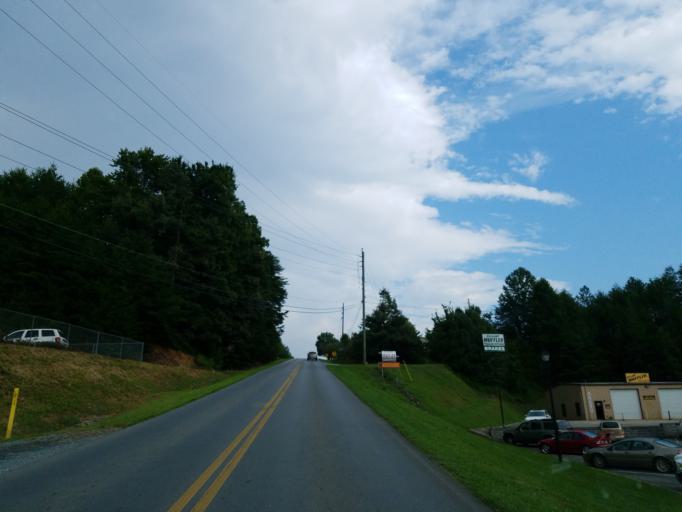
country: US
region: Georgia
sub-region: Gilmer County
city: Ellijay
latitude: 34.6796
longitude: -84.4837
